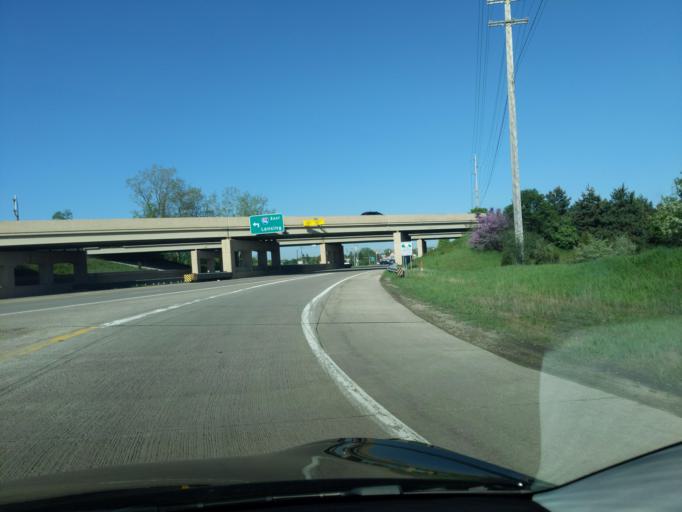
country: US
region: Michigan
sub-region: Kent County
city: Forest Hills
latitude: 42.9131
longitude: -85.5352
